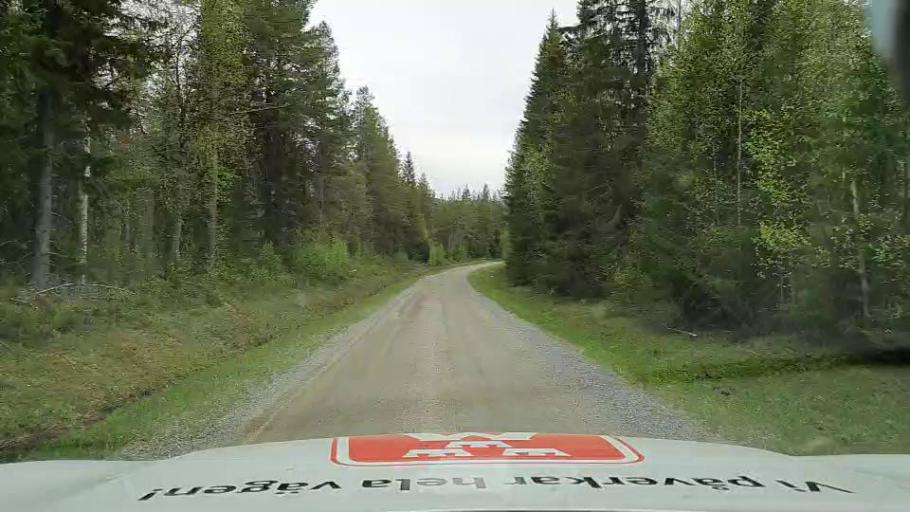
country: SE
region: Jaemtland
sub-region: Bergs Kommun
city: Hoverberg
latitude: 62.5152
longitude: 14.7070
